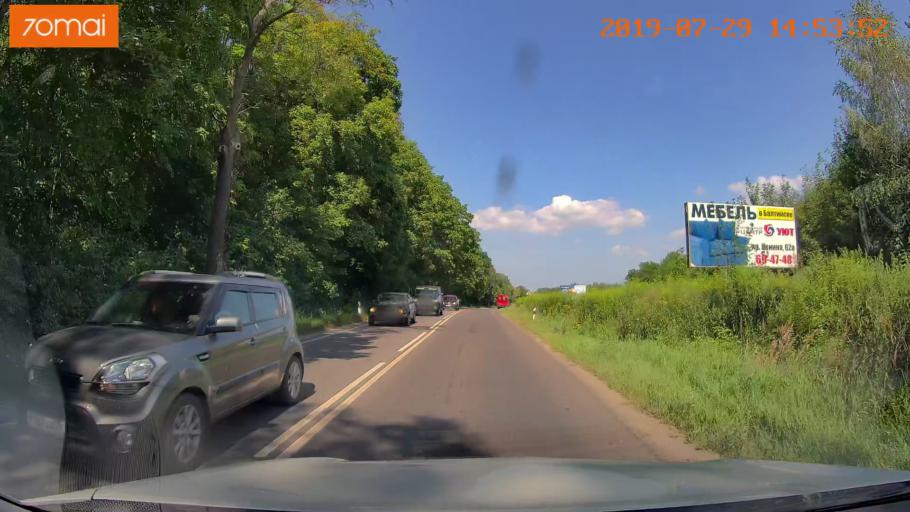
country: RU
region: Kaliningrad
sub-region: Gorod Kaliningrad
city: Baltiysk
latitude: 54.6691
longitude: 19.9205
